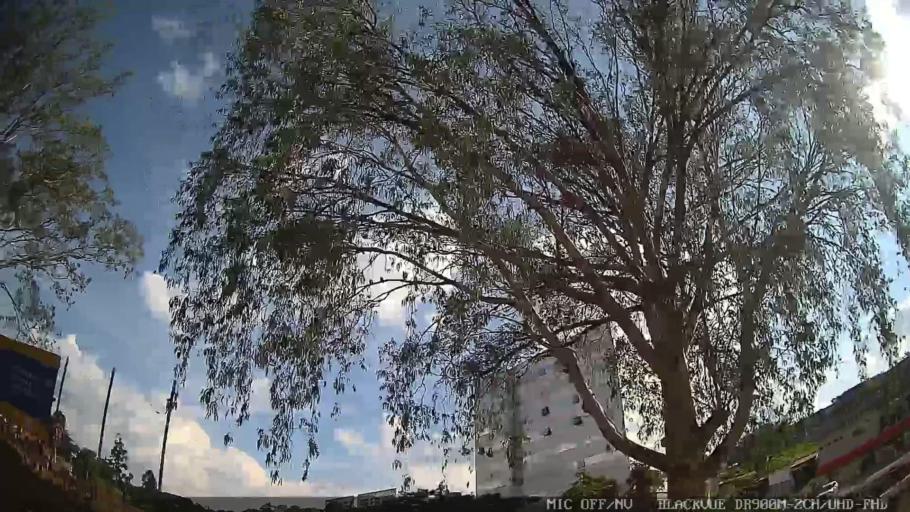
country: BR
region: Sao Paulo
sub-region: Braganca Paulista
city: Braganca Paulista
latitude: -22.9773
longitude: -46.5320
